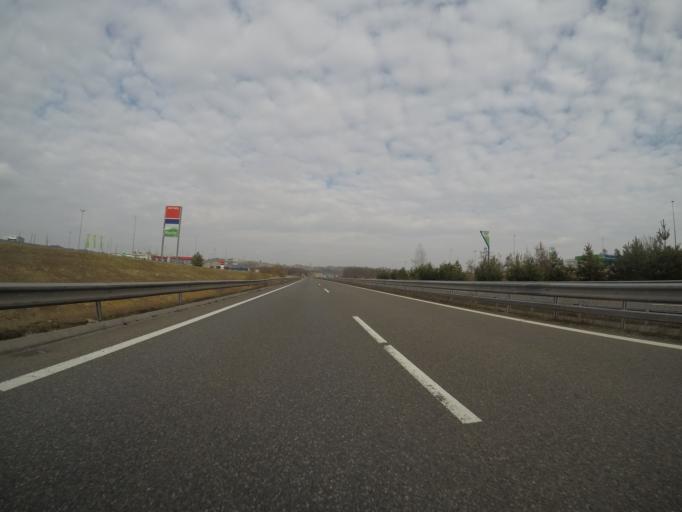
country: SI
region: Sveti Jurij
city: Sveti Jurij ob Scavnici
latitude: 46.5837
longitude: 16.0065
